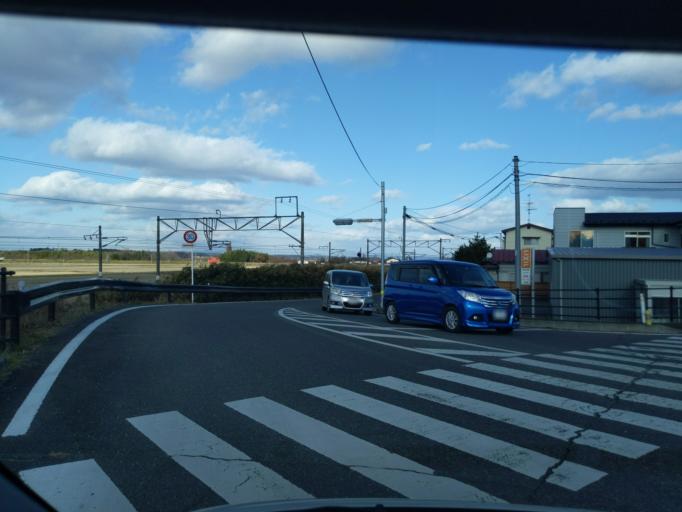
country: JP
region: Miyagi
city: Wakuya
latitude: 38.7100
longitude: 141.1180
